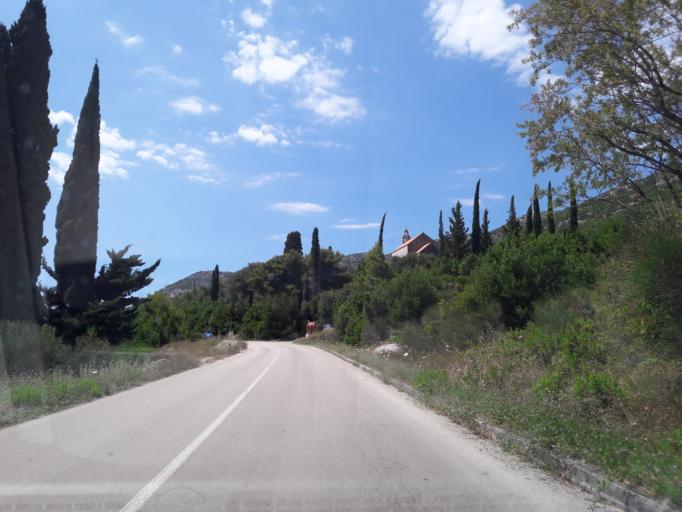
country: HR
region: Dubrovacko-Neretvanska
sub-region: Grad Korcula
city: Zrnovo
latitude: 42.9845
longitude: 17.1014
